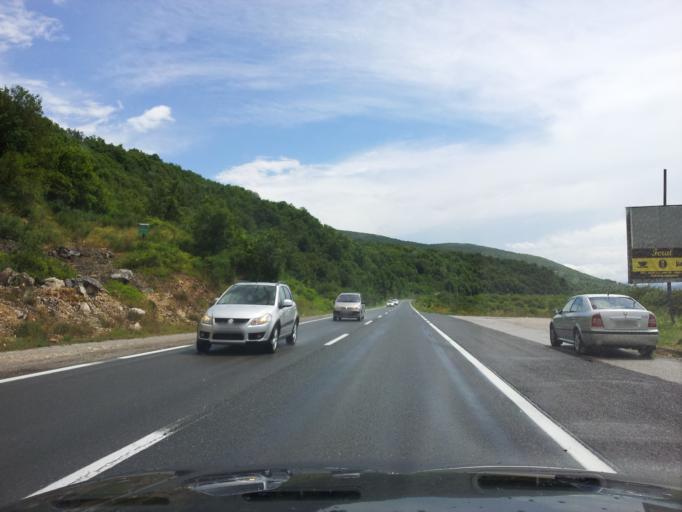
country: BA
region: Federation of Bosnia and Herzegovina
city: Bihac
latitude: 44.6254
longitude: 15.7356
